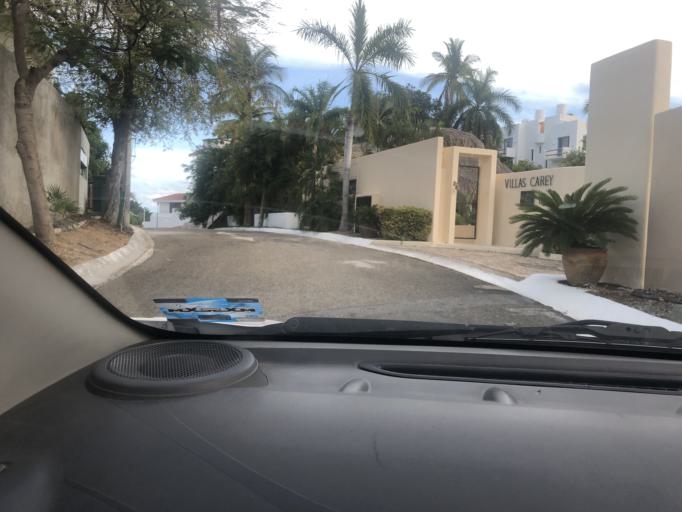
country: MX
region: Oaxaca
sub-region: Santa Maria Huatulco
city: Crucecita
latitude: 15.7726
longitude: -96.0890
